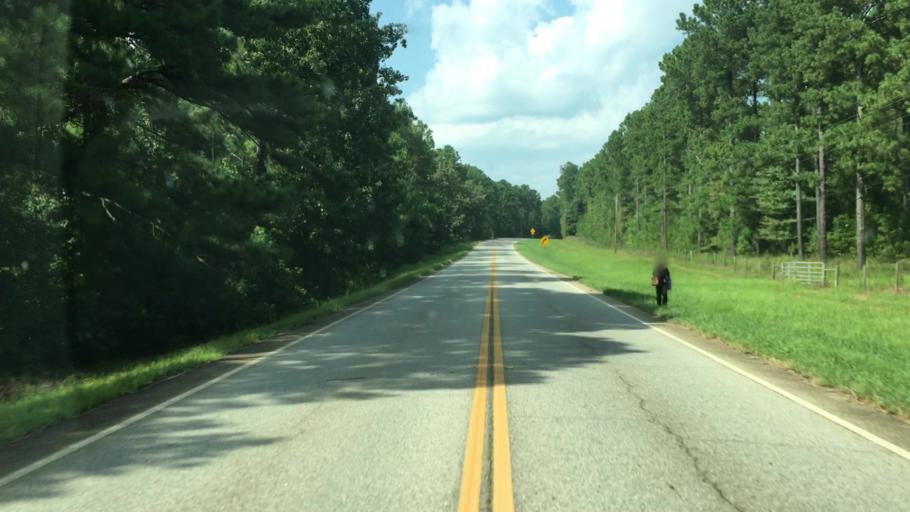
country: US
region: Georgia
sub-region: Monroe County
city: Forsyth
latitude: 33.1273
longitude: -83.8718
